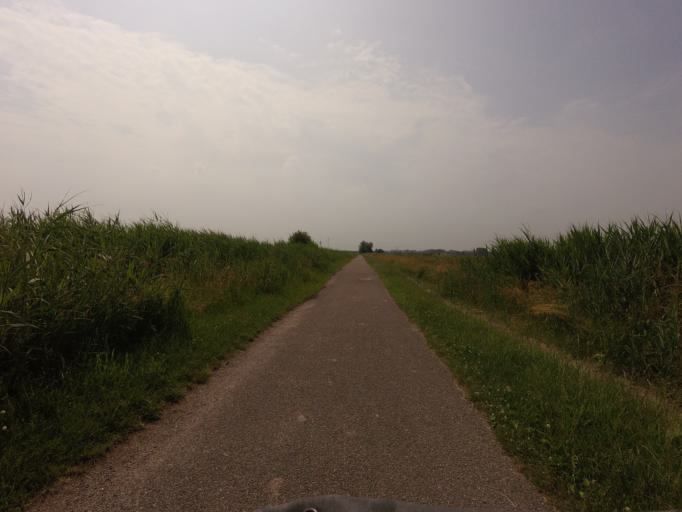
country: NL
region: South Holland
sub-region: Gemeente Krimpen aan den IJssel
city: Krimpen aan den IJssel
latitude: 51.9544
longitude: 4.6317
